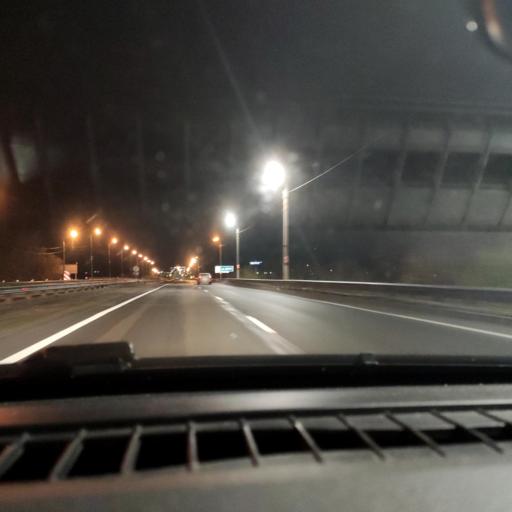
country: RU
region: Voronezj
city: Pridonskoy
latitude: 51.6506
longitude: 39.0715
